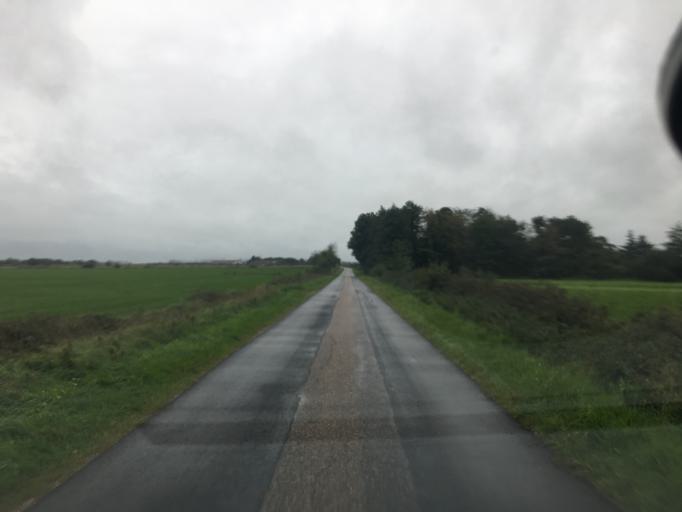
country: DE
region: Schleswig-Holstein
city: Ellhoft
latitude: 54.9474
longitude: 9.0053
